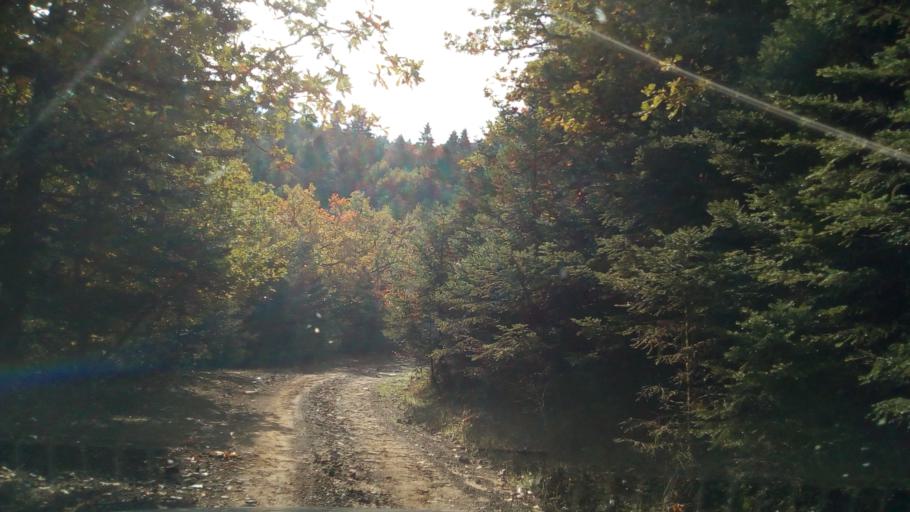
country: GR
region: Central Greece
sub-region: Nomos Fokidos
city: Lidoriki
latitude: 38.4811
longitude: 22.0548
